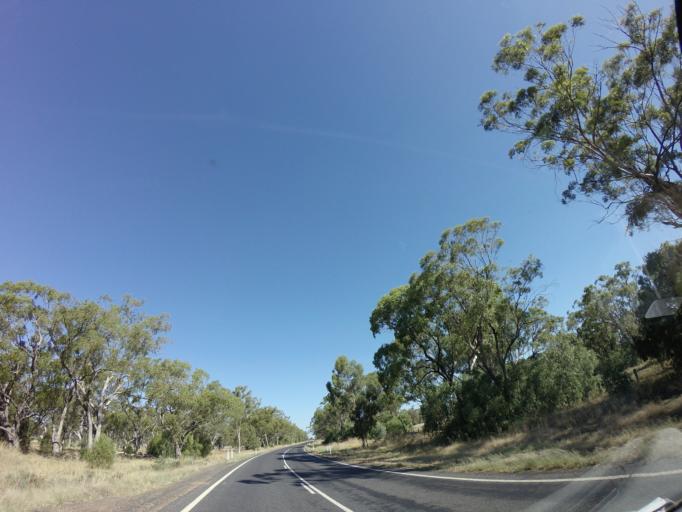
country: AU
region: New South Wales
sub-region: Narromine
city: Narromine
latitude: -31.6426
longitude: 147.9118
